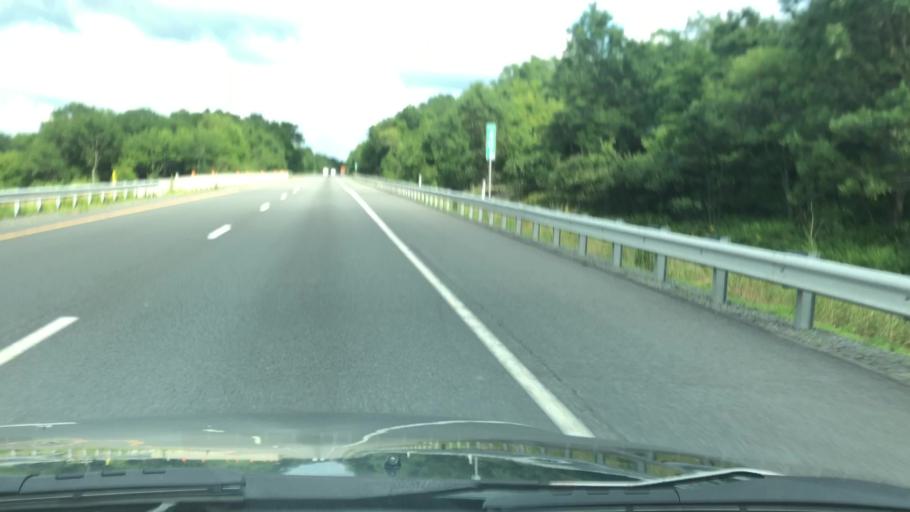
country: US
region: Pennsylvania
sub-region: Pike County
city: Gold Key Lake
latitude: 41.3485
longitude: -74.9412
